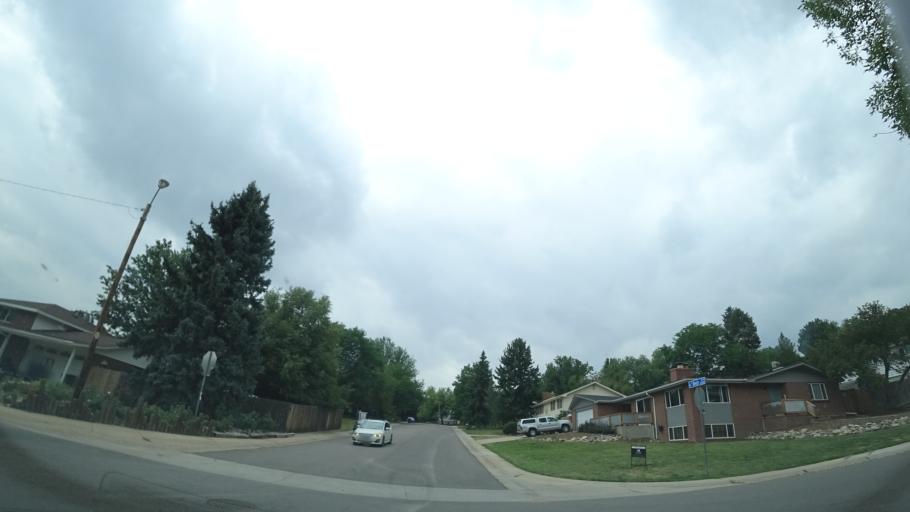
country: US
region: Colorado
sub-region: Jefferson County
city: West Pleasant View
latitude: 39.6979
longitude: -105.1497
